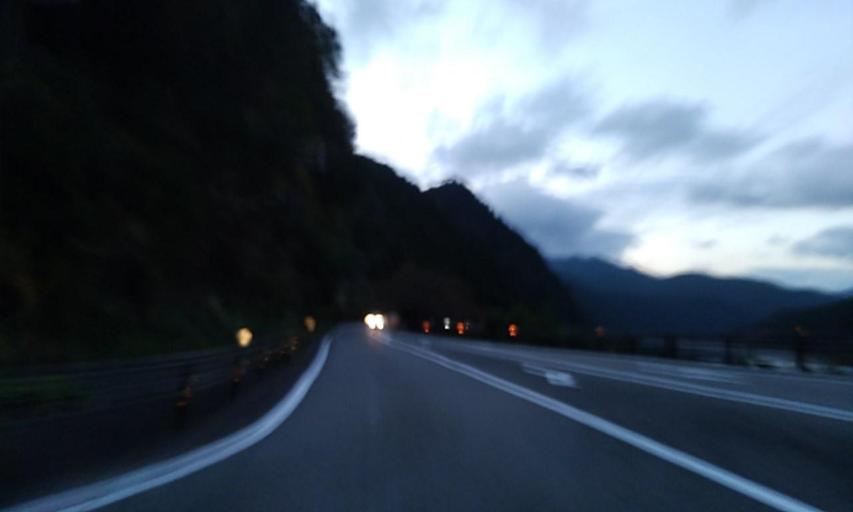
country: JP
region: Wakayama
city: Shingu
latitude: 33.7266
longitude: 135.9539
